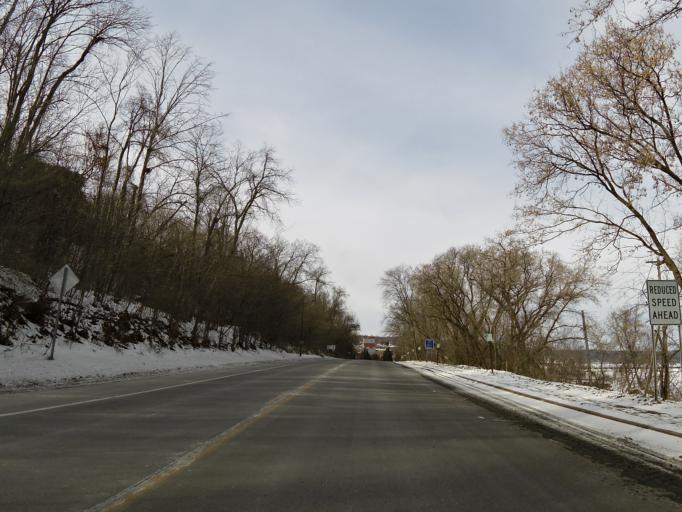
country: US
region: Minnesota
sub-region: Washington County
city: Stillwater
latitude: 45.0510
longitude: -92.8016
